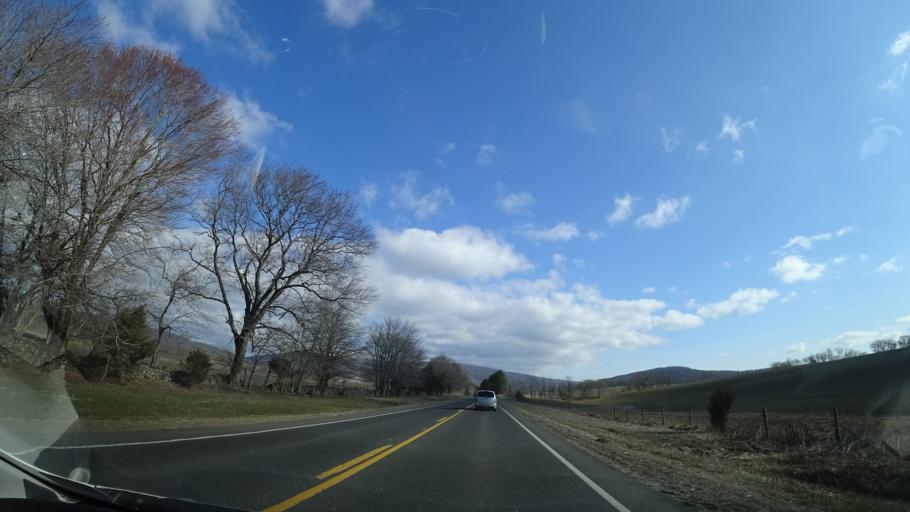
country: US
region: Virginia
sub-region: Warren County
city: Shenandoah Farms
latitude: 38.9798
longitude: -77.9508
